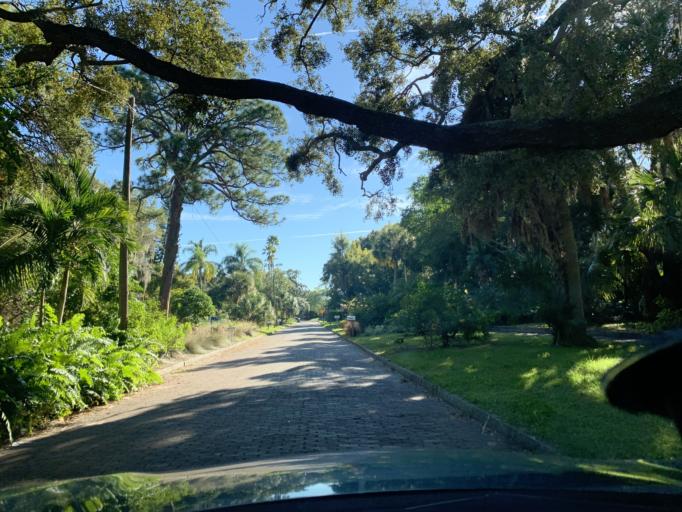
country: US
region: Florida
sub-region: Pinellas County
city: Gulfport
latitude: 27.7400
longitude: -82.7011
